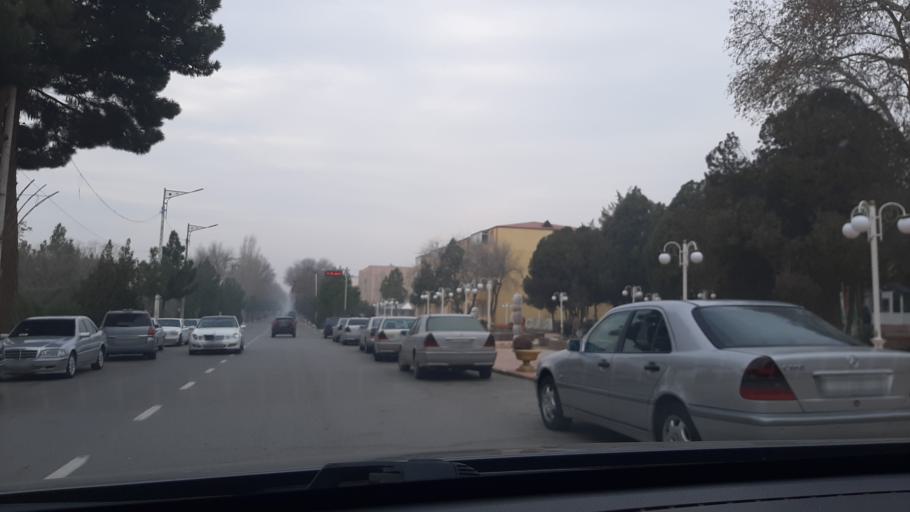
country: TJ
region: Viloyati Sughd
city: Palos
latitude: 40.2667
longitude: 69.8006
